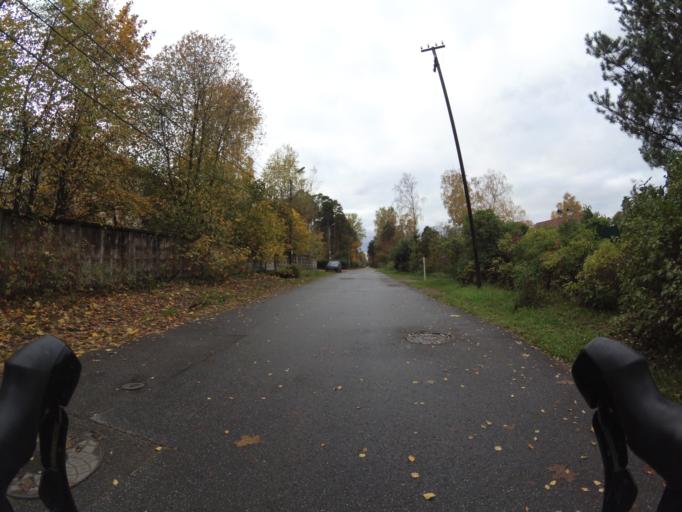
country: RU
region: St.-Petersburg
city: Lakhtinskiy
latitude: 60.0011
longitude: 30.1512
